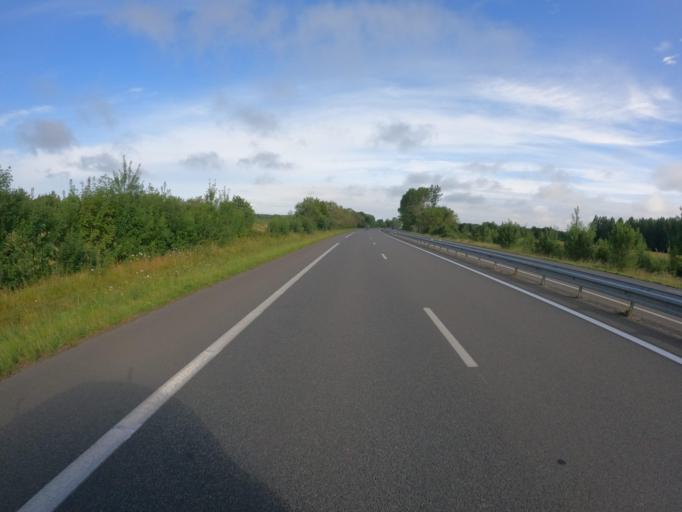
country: FR
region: Pays de la Loire
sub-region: Departement de Maine-et-Loire
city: Vivy
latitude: 47.2970
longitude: -0.0270
